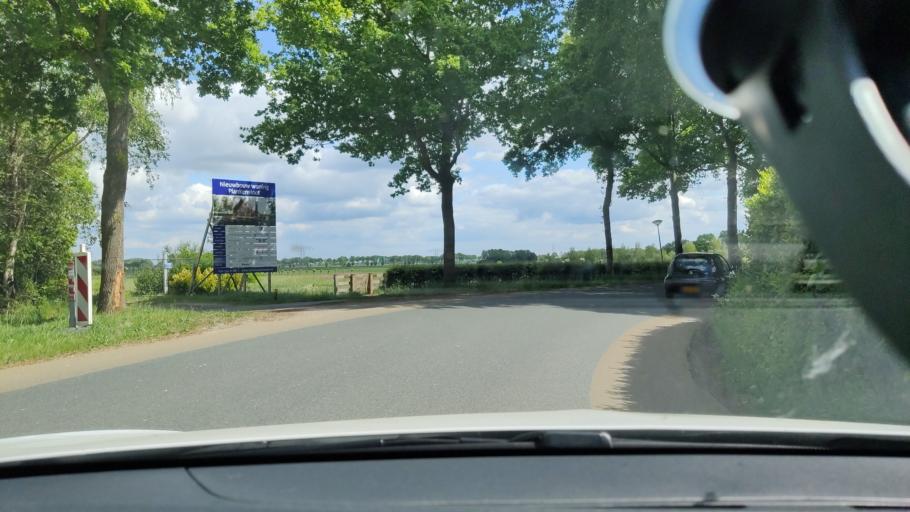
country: NL
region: Drenthe
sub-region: Gemeente Tynaarlo
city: Zuidlaren
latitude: 53.1083
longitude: 6.6830
